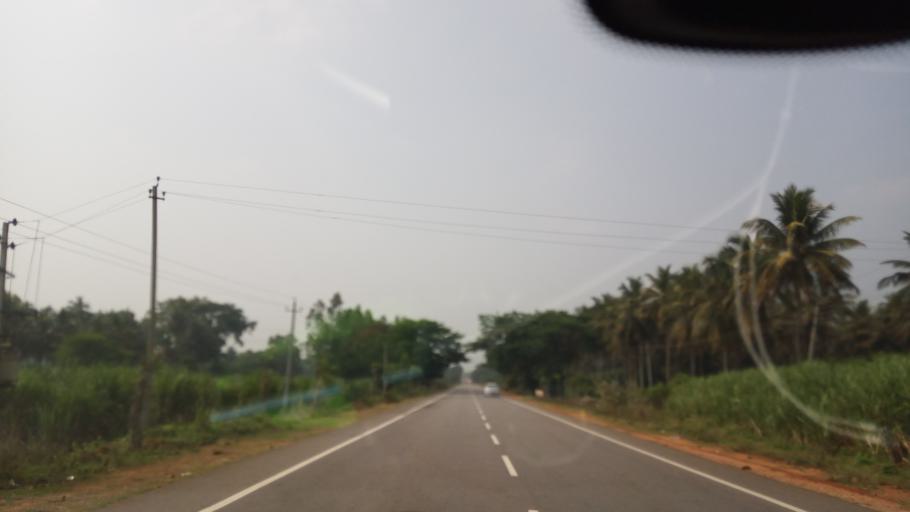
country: IN
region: Karnataka
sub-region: Mandya
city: Pandavapura
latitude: 12.5364
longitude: 76.6704
